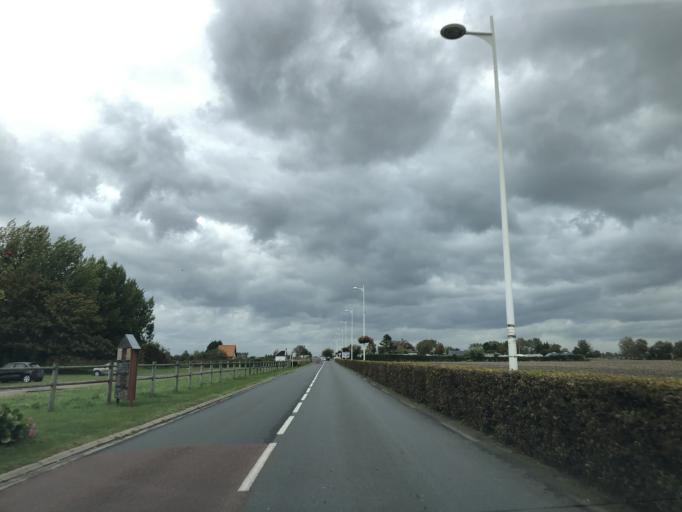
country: FR
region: Picardie
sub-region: Departement de la Somme
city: Le Crotoy
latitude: 50.2206
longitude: 1.6309
